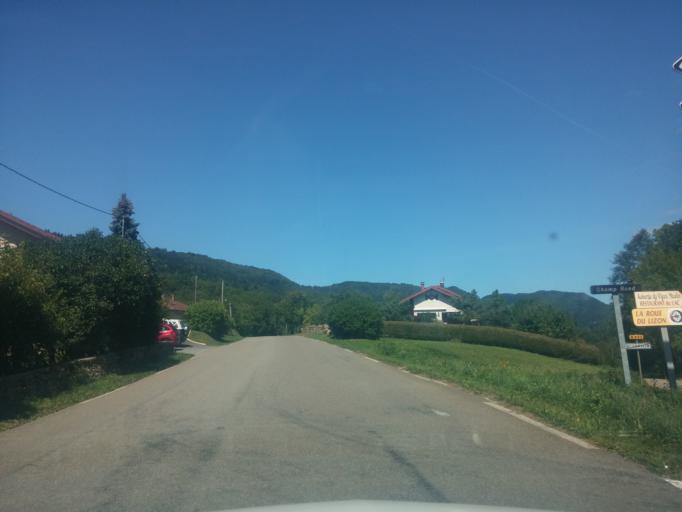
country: FR
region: Franche-Comte
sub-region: Departement du Jura
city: Saint-Lupicin
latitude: 46.4099
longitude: 5.7952
